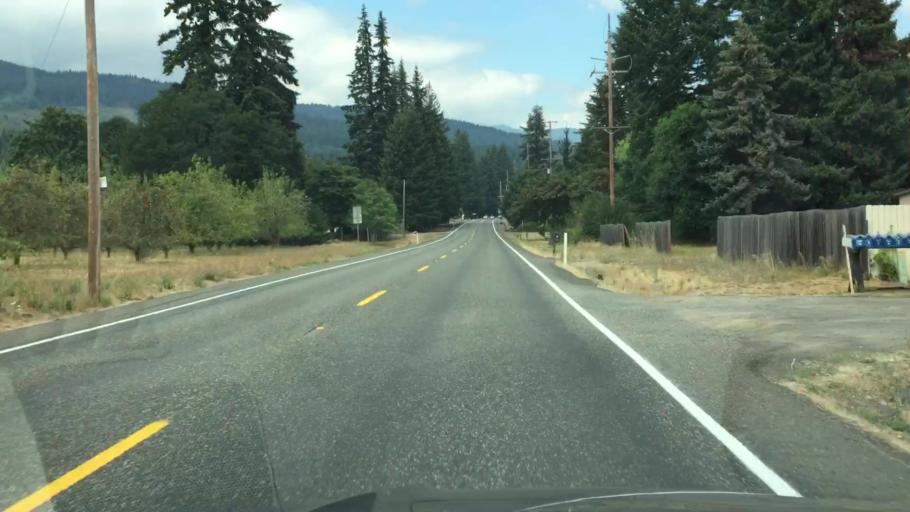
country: US
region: Washington
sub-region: Klickitat County
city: White Salmon
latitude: 45.8469
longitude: -121.5072
